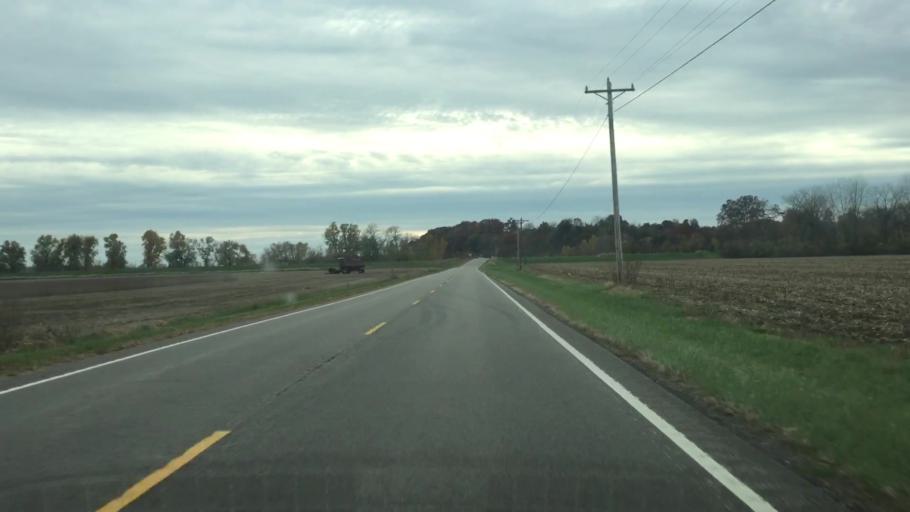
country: US
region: Missouri
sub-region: Callaway County
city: Fulton
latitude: 38.6990
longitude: -91.8221
